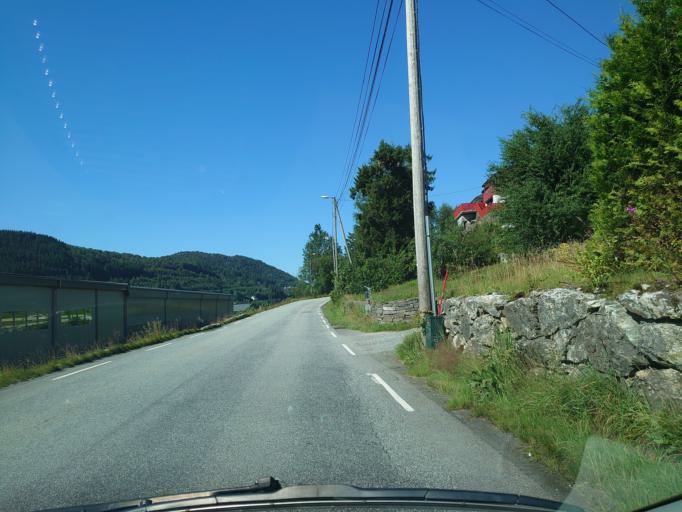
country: NO
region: Hordaland
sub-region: Bergen
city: Indre Arna
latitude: 60.4341
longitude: 5.4638
